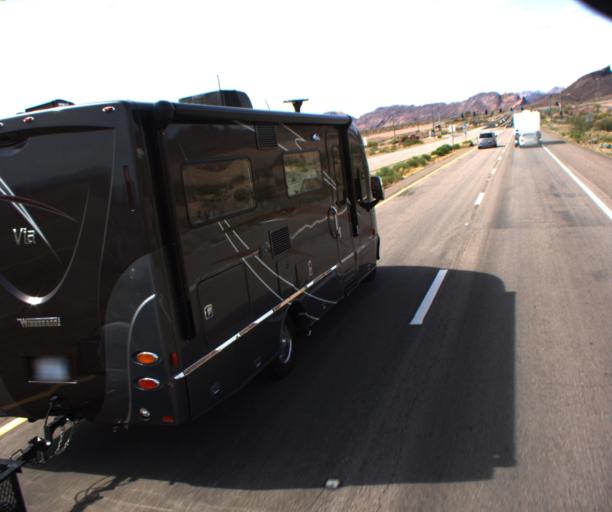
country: US
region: Arizona
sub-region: Mohave County
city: Desert Hills
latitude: 34.5773
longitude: -114.3662
